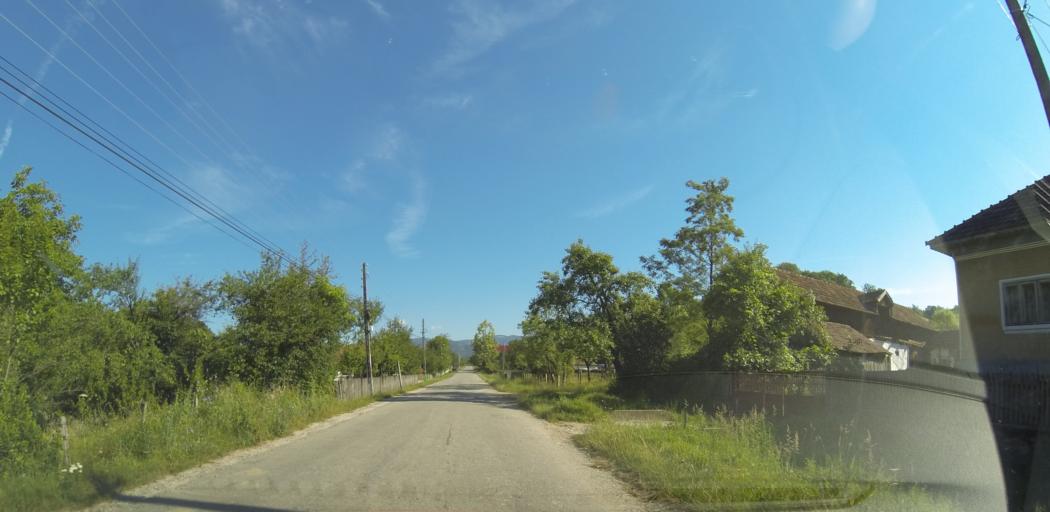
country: RO
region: Valcea
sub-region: Comuna Slatioara
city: Slatioara
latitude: 45.1525
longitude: 23.8675
